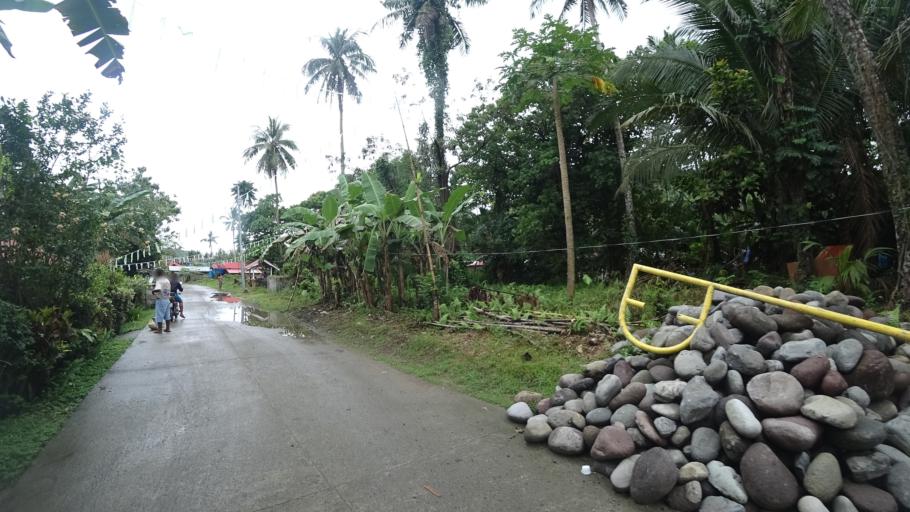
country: PH
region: Eastern Visayas
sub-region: Province of Leyte
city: Bugho
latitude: 10.7975
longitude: 124.9714
